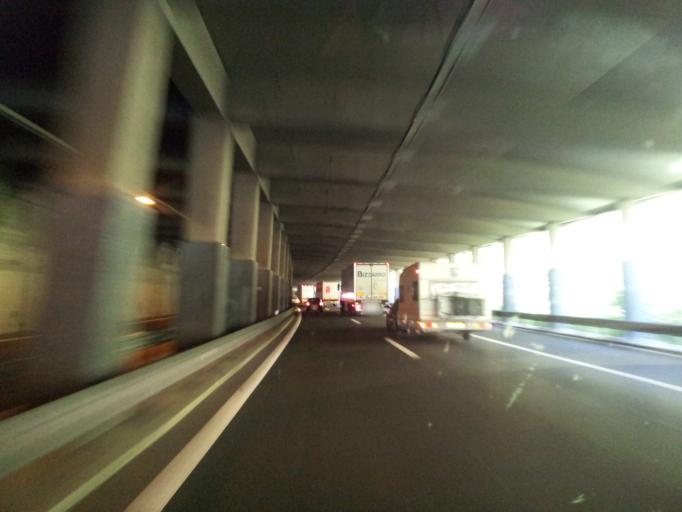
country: CH
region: Uri
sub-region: Uri
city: Andermatt
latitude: 46.7175
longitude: 8.6148
